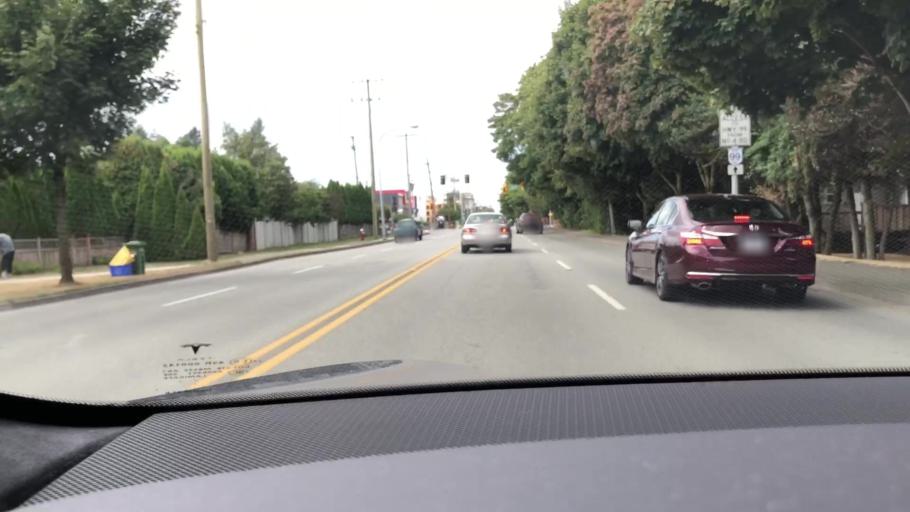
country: CA
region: British Columbia
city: Richmond
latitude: 49.1847
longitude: -123.1124
